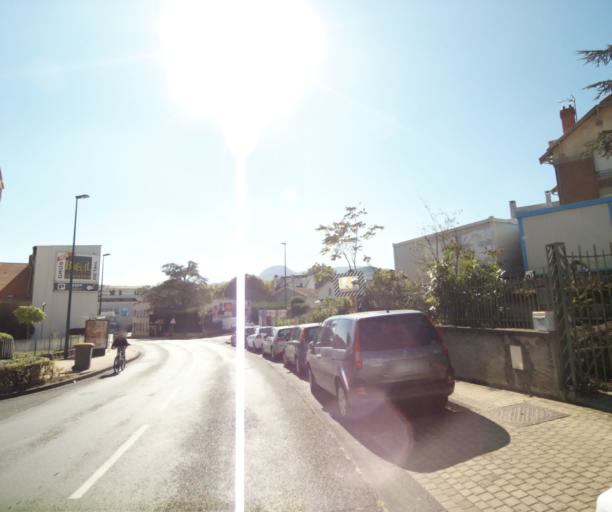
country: FR
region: Auvergne
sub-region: Departement du Puy-de-Dome
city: Chamalieres
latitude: 45.7797
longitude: 3.0623
